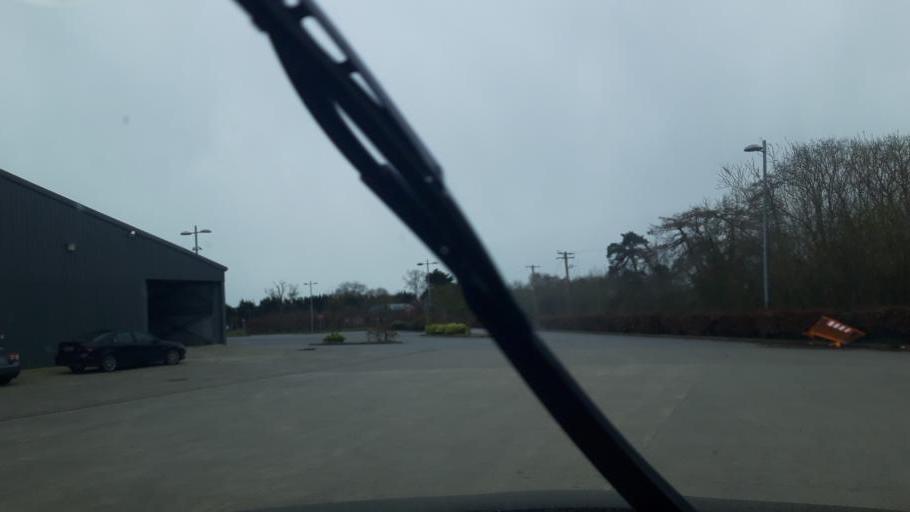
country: IE
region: Leinster
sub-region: Kilkenny
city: Kilkenny
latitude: 52.6516
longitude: -7.2121
